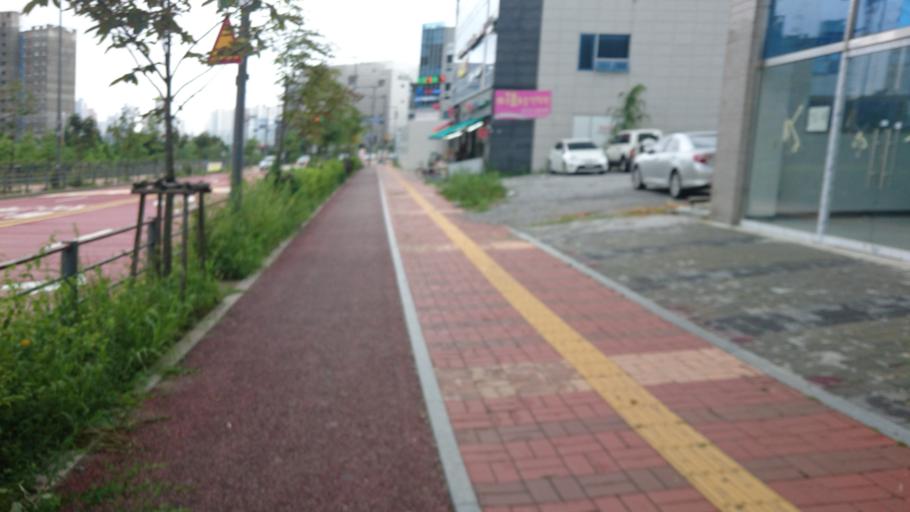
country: KR
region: Gyeonggi-do
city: Suwon-si
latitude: 37.3051
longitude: 127.0474
